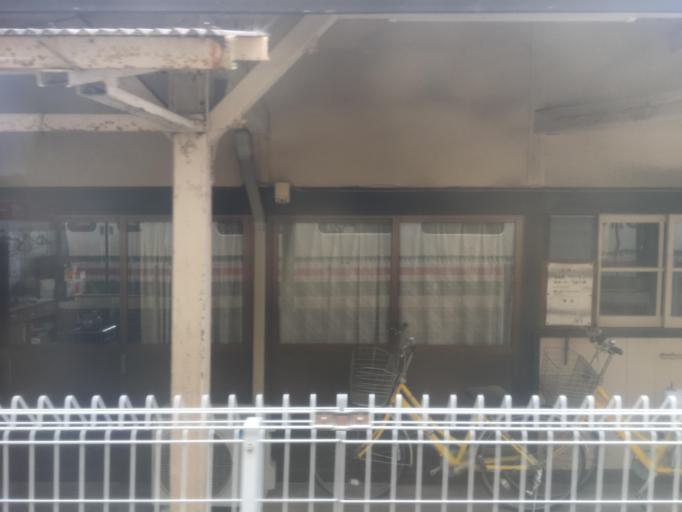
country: JP
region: Gunma
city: Tomioka
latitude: 36.2531
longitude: 138.8638
